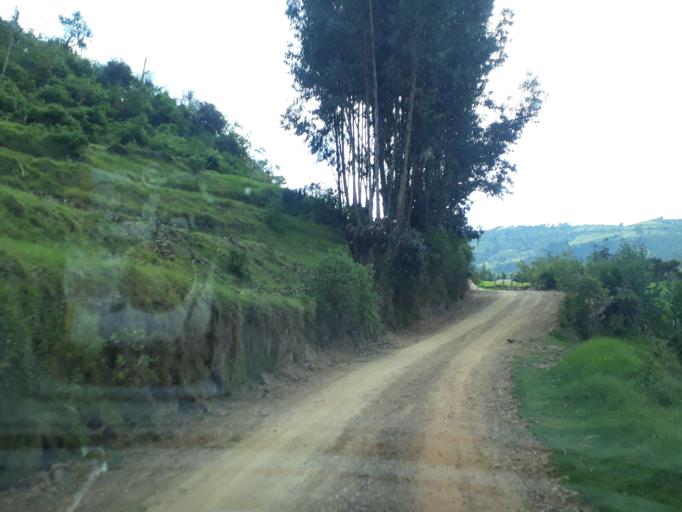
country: CO
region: Boyaca
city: Santa Rosa de Viterbo
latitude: 5.8517
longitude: -72.9609
